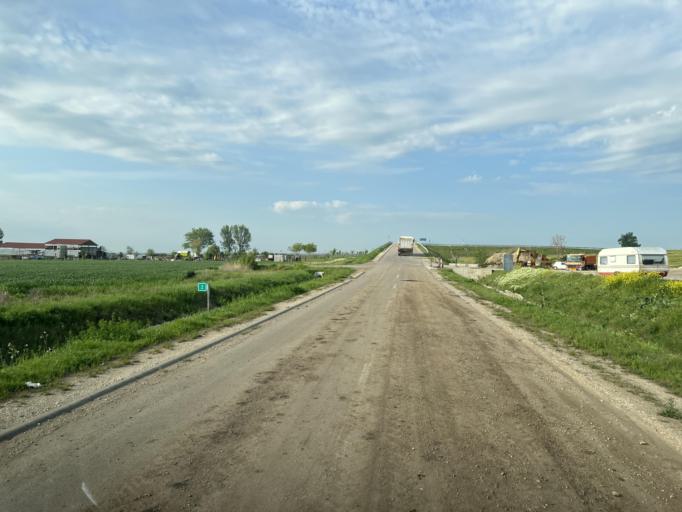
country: HU
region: Pest
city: Cegledbercel
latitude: 47.2249
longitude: 19.6967
